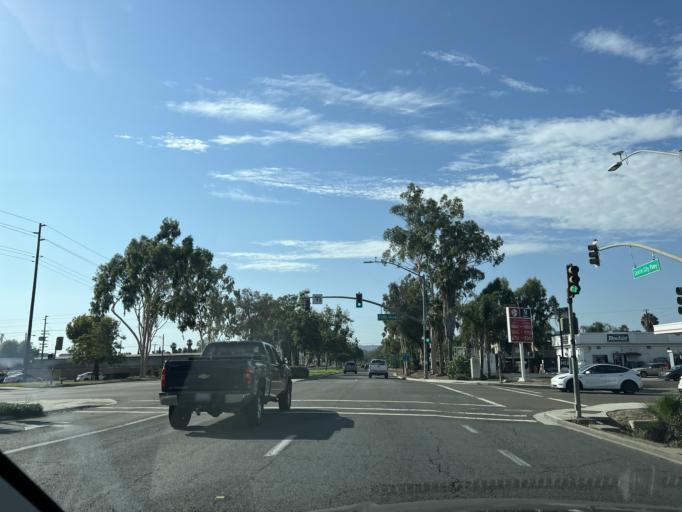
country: US
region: California
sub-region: San Diego County
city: Escondido
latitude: 33.1153
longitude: -117.0839
